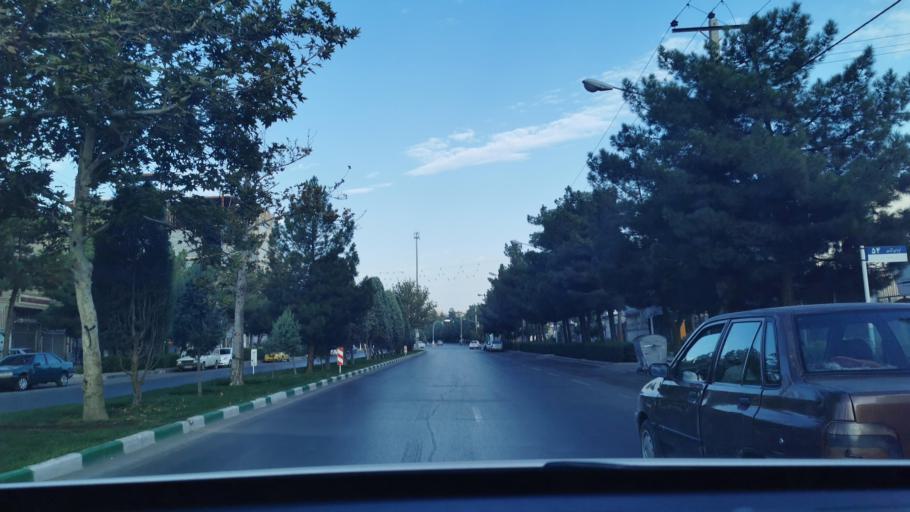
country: IR
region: Razavi Khorasan
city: Mashhad
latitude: 36.3593
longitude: 59.5094
